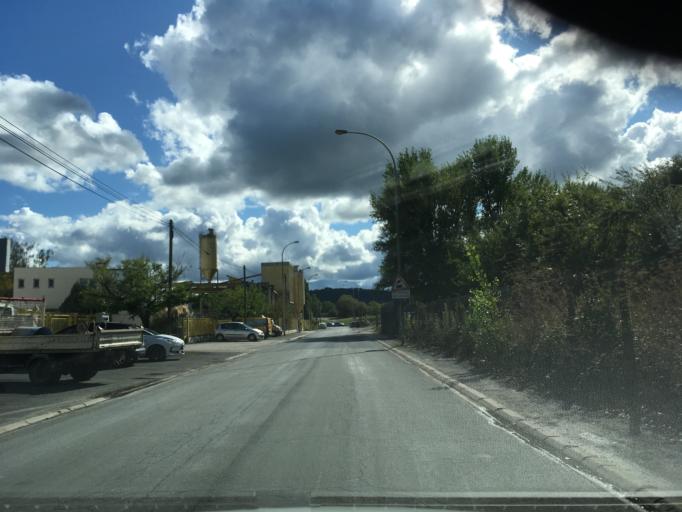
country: FR
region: Limousin
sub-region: Departement de la Correze
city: Saint-Pantaleon-de-Larche
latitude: 45.1514
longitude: 1.4781
